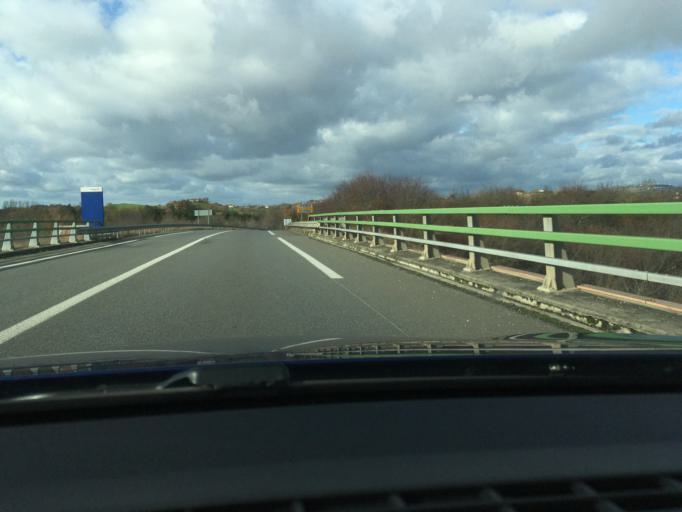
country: FR
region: Midi-Pyrenees
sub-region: Departement du Tarn-et-Garonne
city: Caussade
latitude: 44.1451
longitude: 1.5181
